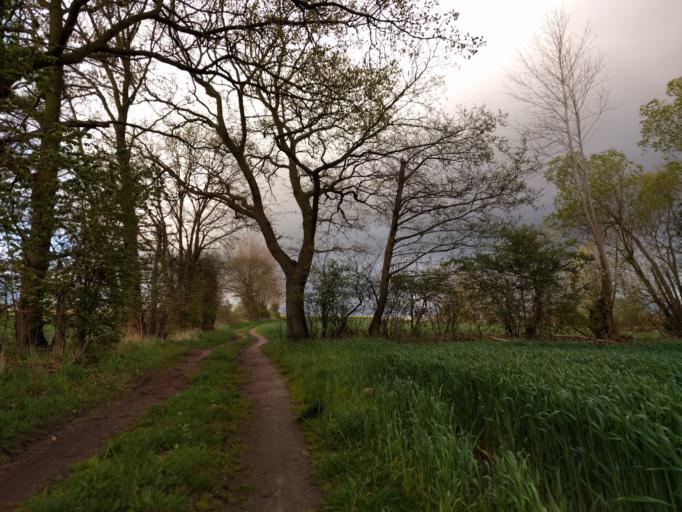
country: DK
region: South Denmark
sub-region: Kerteminde Kommune
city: Munkebo
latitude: 55.4301
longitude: 10.5227
